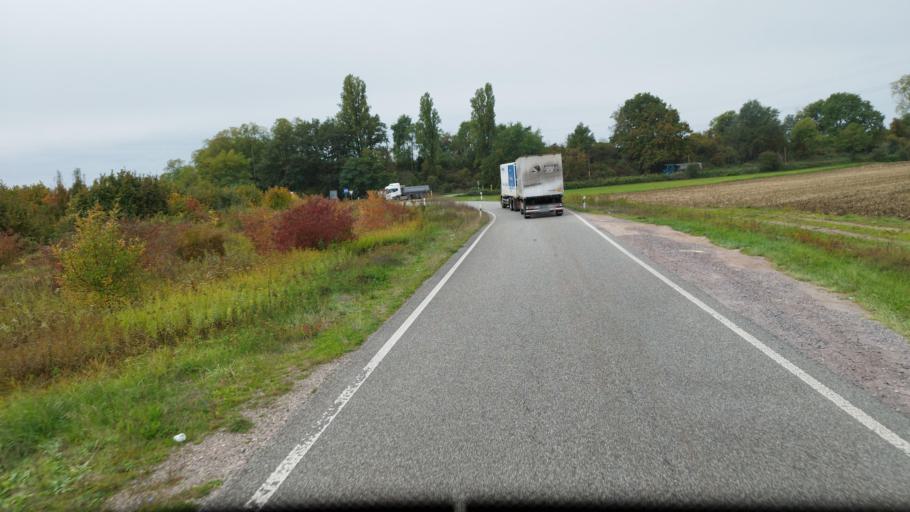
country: DE
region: Rheinland-Pfalz
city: Neupotz
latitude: 49.1004
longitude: 8.3032
